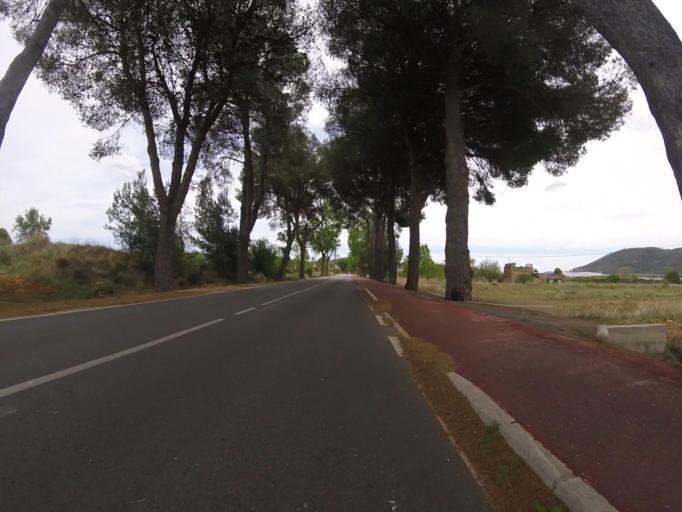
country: ES
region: Valencia
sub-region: Provincia de Castello
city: Cabanes
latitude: 40.1649
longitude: 0.0167
